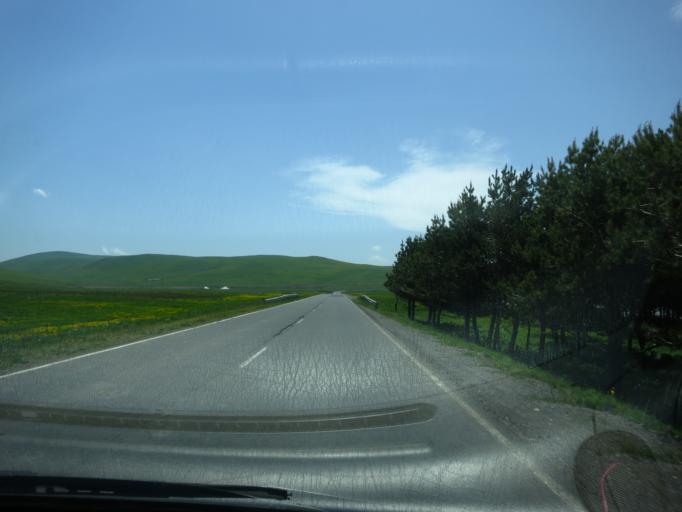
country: GE
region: Samtskhe-Javakheti
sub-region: Ninotsminda
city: Ninotsminda
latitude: 41.3021
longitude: 43.7574
